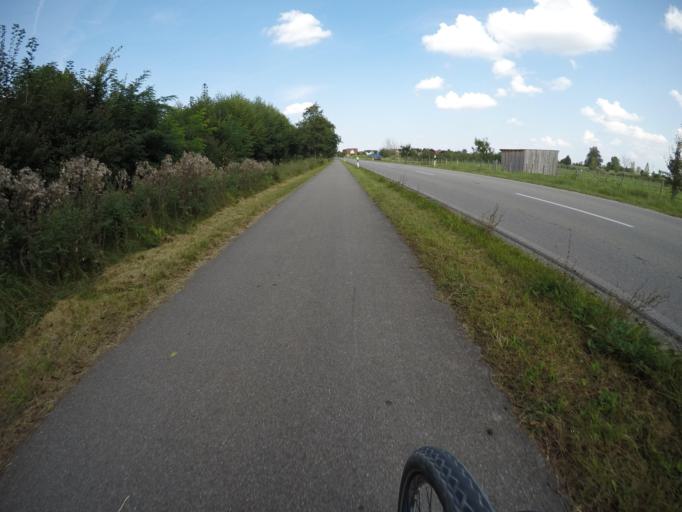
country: DE
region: Bavaria
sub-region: Swabia
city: Kuhlenthal
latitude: 48.5569
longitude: 10.8196
